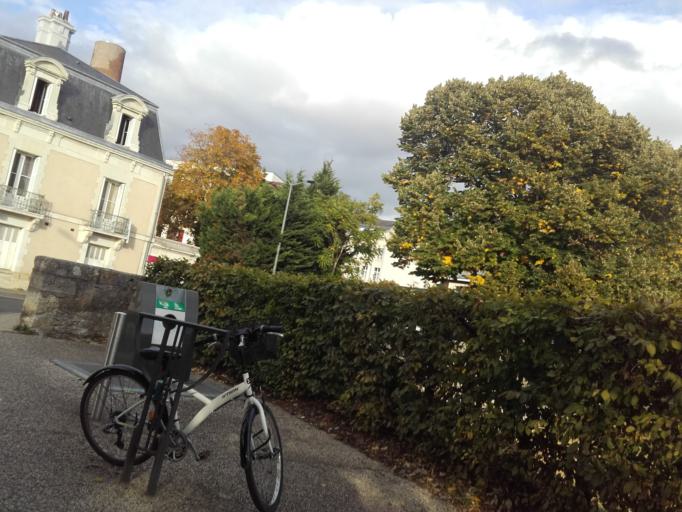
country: FR
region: Centre
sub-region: Departement d'Indre-et-Loire
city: Saint-Cyr-sur-Loire
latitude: 47.4003
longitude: 0.6794
